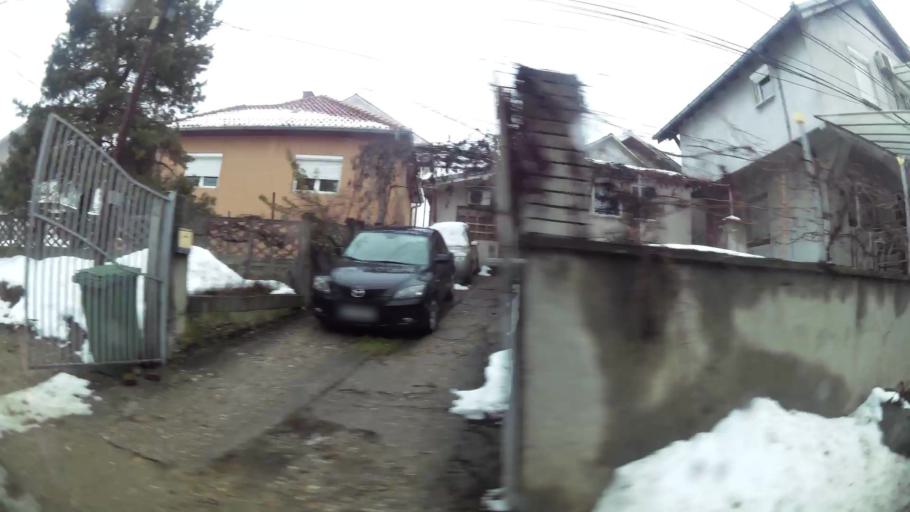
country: RS
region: Central Serbia
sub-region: Belgrade
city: Zvezdara
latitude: 44.7759
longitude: 20.5312
